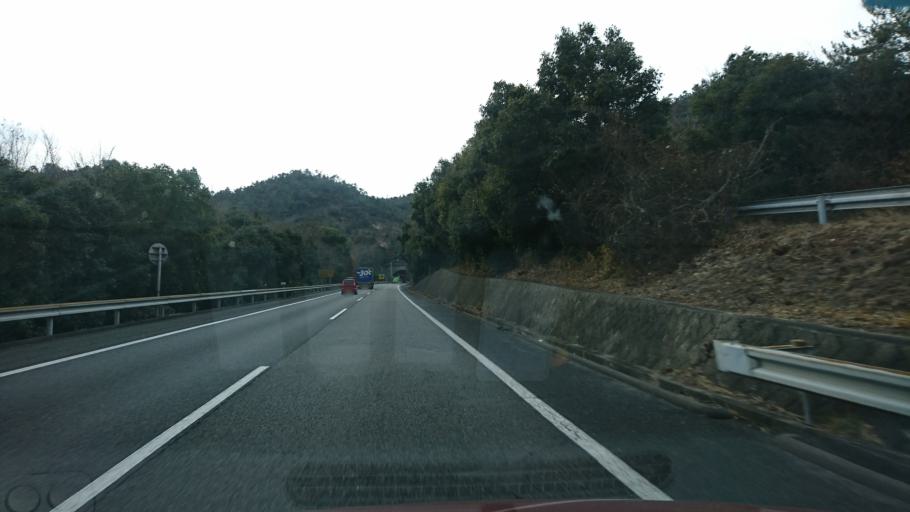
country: JP
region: Okayama
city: Kurashiki
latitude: 34.6148
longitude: 133.7386
